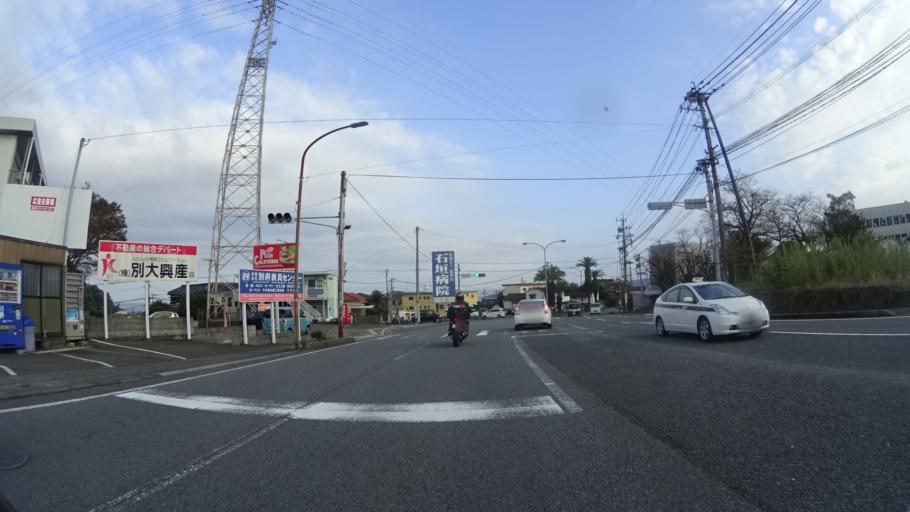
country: JP
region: Oita
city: Beppu
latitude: 33.3117
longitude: 131.4851
